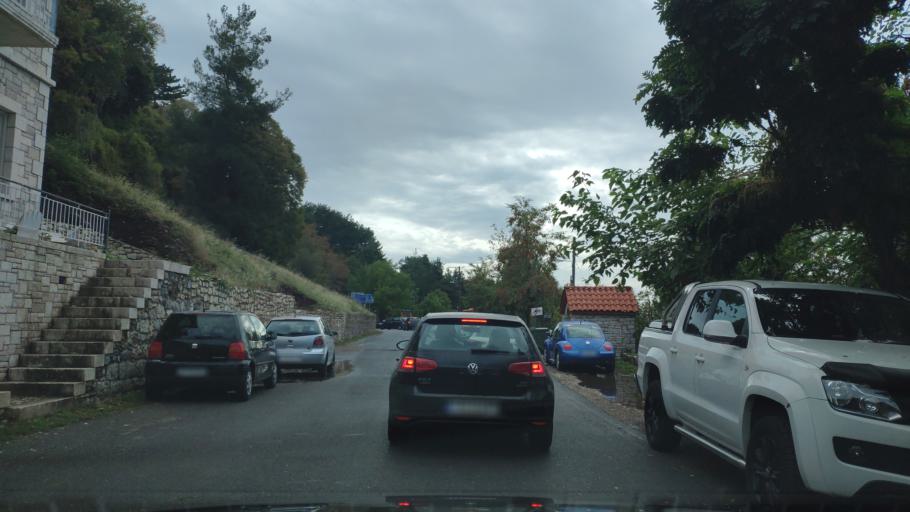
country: GR
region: Peloponnese
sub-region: Nomos Arkadias
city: Dimitsana
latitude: 37.5931
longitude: 22.0418
